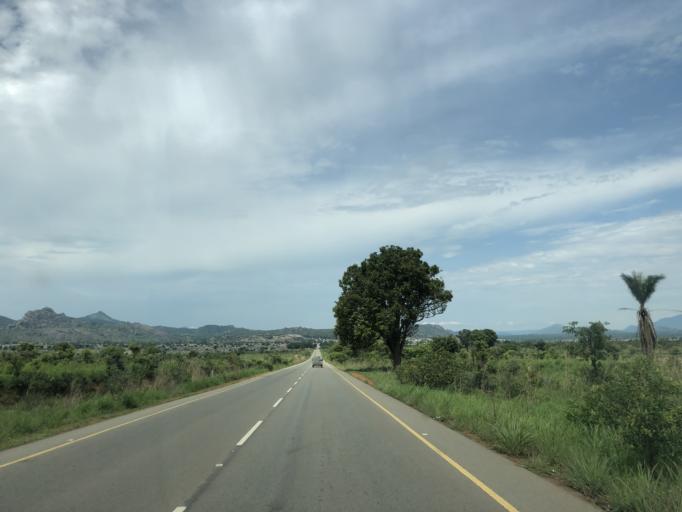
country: AO
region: Cuanza Sul
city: Quibala
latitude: -10.7341
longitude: 15.0100
